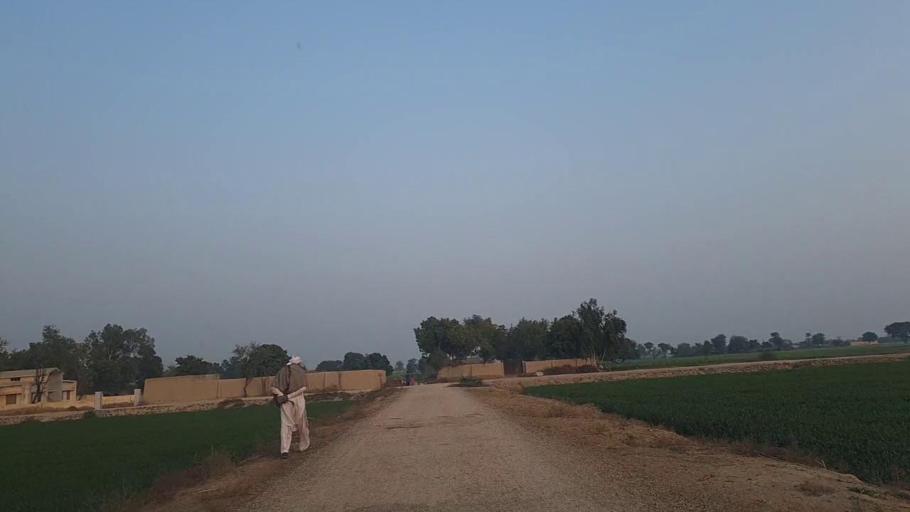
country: PK
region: Sindh
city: Nawabshah
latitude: 26.2693
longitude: 68.4561
